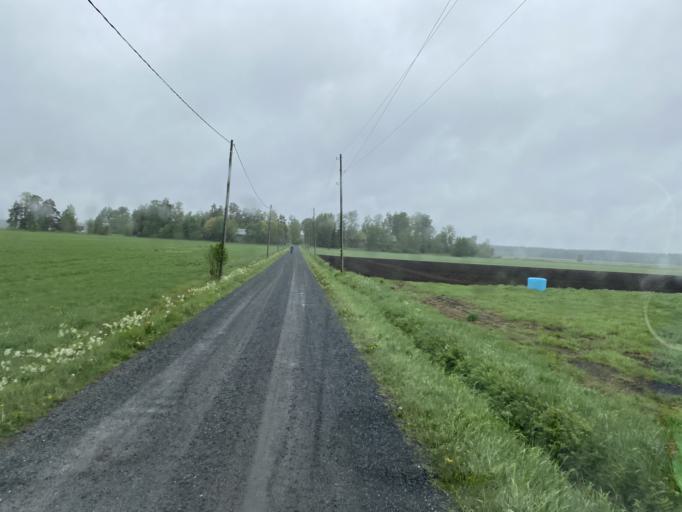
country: FI
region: Pirkanmaa
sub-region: Etelae-Pirkanmaa
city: Urjala
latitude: 60.9515
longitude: 23.5515
